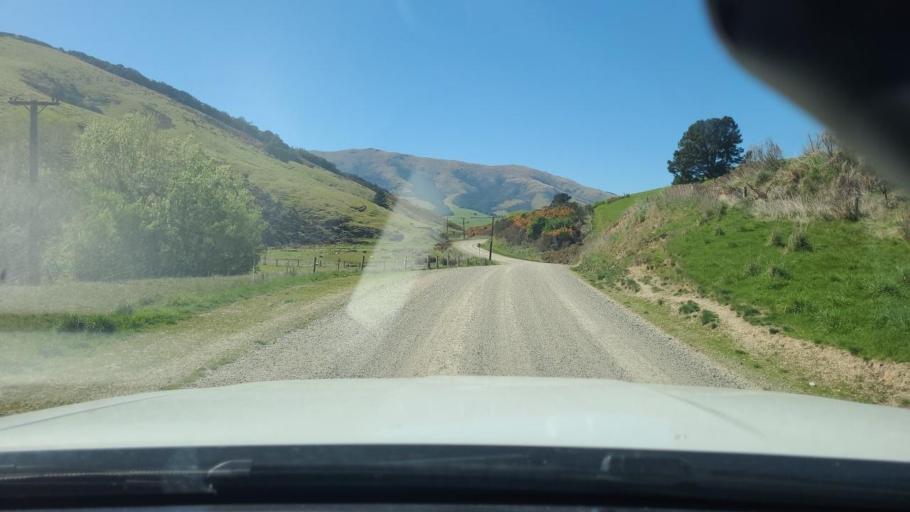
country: NZ
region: Southland
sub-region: Gore District
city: Gore
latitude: -45.7543
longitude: 168.9255
